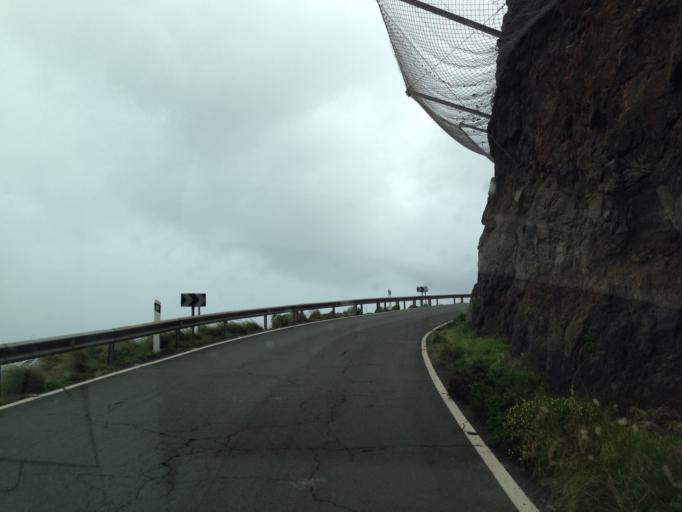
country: ES
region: Canary Islands
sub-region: Provincia de Las Palmas
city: San Nicolas
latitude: 28.0319
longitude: -15.7633
